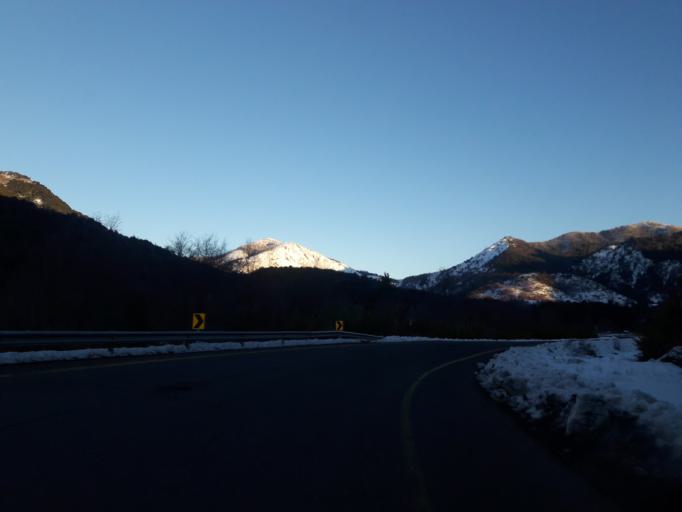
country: CL
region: Araucania
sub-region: Provincia de Cautin
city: Vilcun
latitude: -38.4954
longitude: -71.5209
